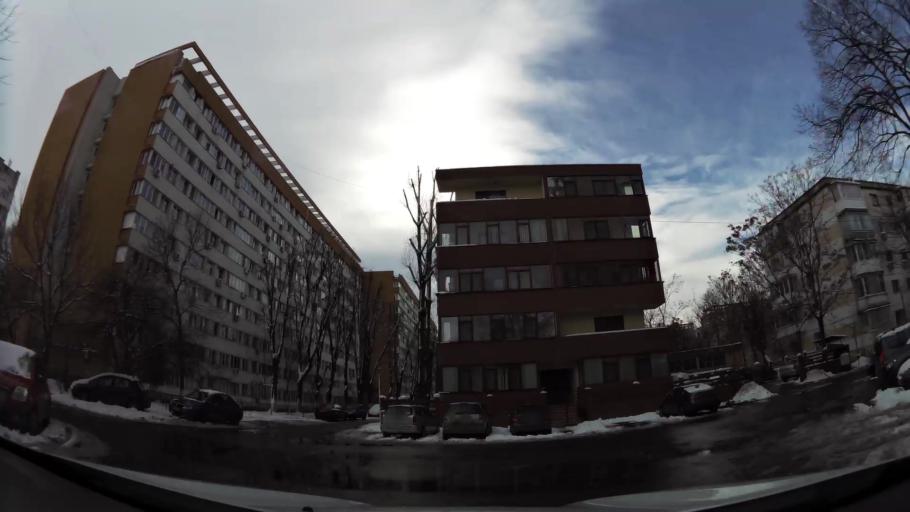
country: RO
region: Ilfov
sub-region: Comuna Popesti-Leordeni
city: Popesti-Leordeni
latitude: 44.3789
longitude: 26.1224
